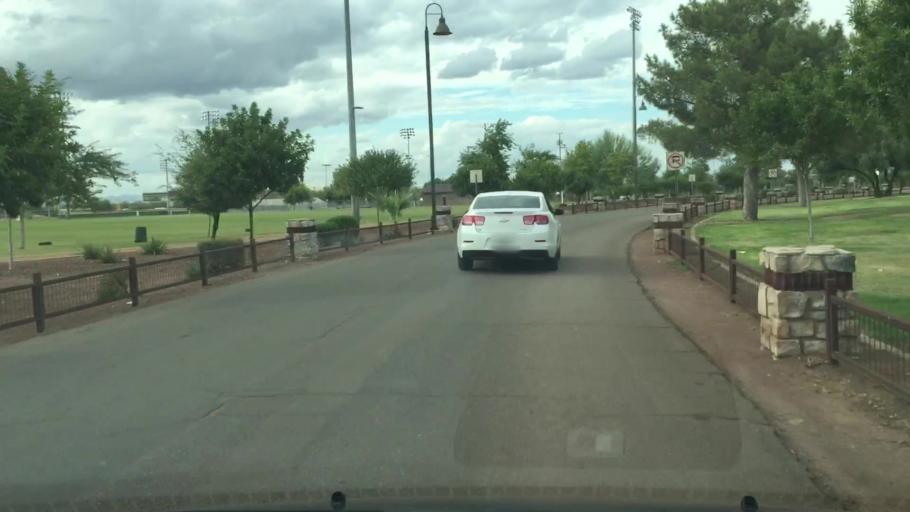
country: US
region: Arizona
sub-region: Maricopa County
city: Laveen
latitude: 33.3716
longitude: -112.1417
